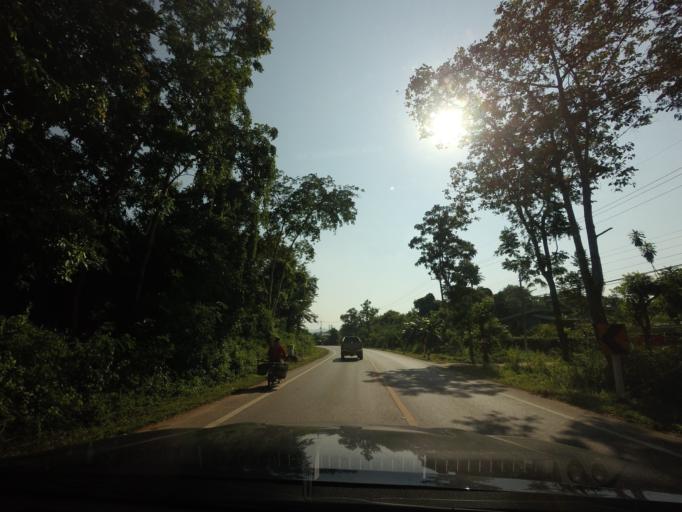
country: TH
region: Nan
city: Nan
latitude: 18.8099
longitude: 100.8014
